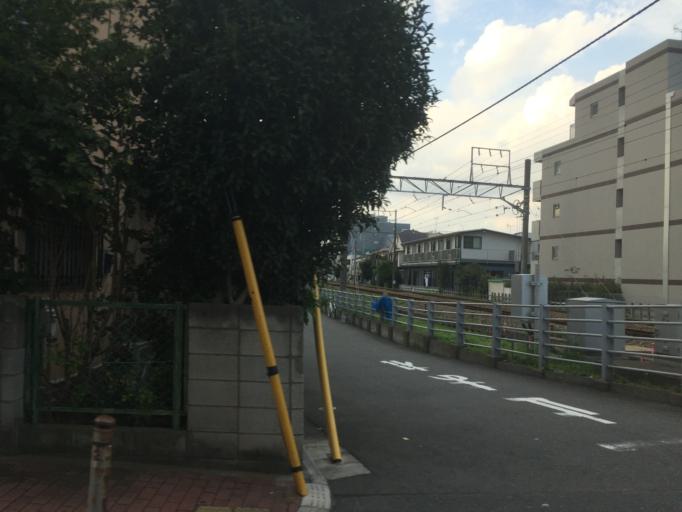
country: JP
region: Kanagawa
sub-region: Kawasaki-shi
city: Kawasaki
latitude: 35.5724
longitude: 139.6838
